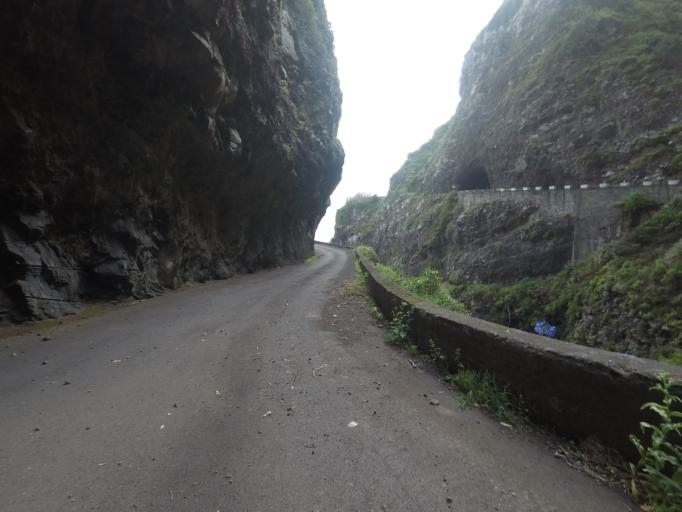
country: PT
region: Madeira
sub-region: Sao Vicente
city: Sao Vicente
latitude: 32.8113
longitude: -17.0661
